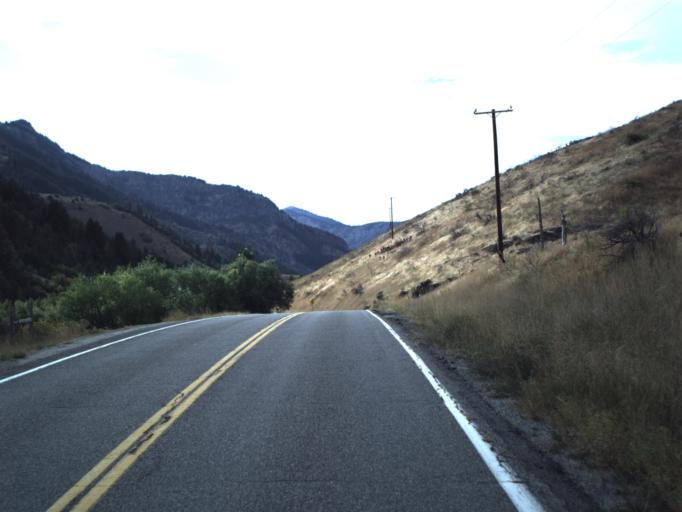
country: US
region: Utah
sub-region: Cache County
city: Millville
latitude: 41.6163
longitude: -111.6399
